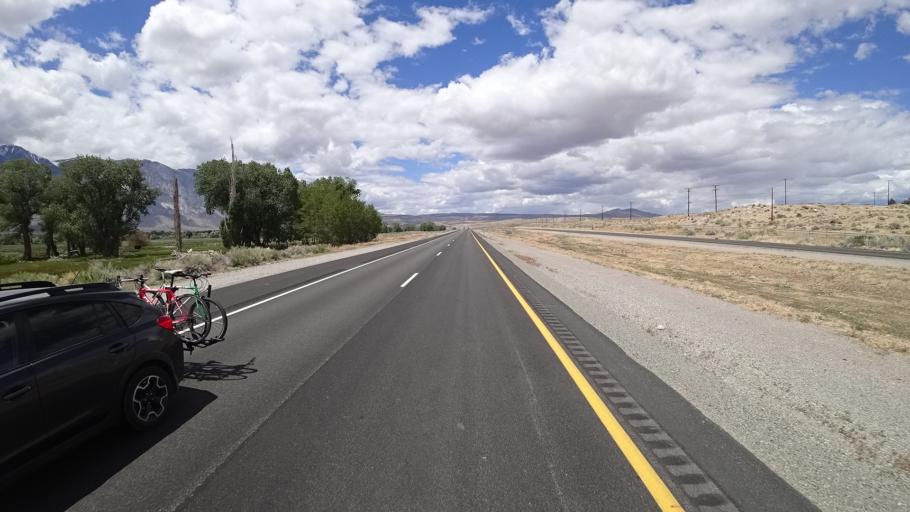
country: US
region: California
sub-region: Inyo County
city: West Bishop
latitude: 37.4133
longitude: -118.5524
